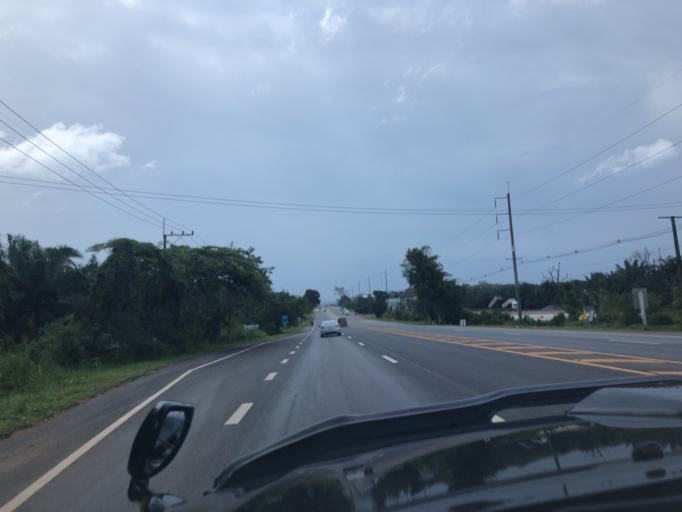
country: TH
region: Phangnga
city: Ban Ao Nang
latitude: 8.2097
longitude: 98.8130
